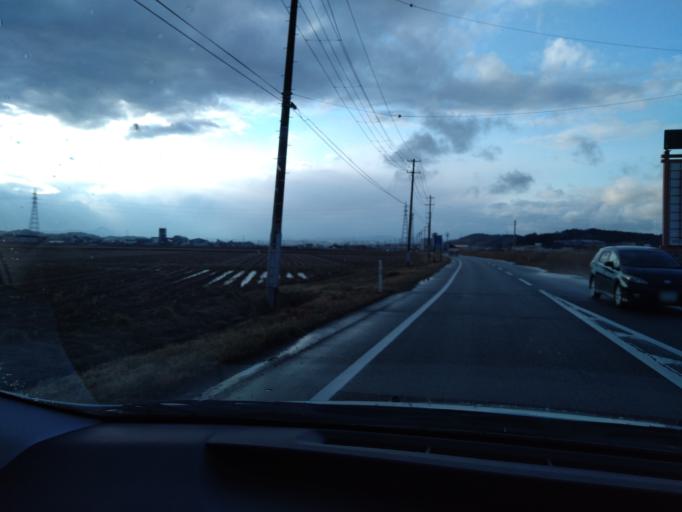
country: JP
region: Iwate
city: Ichinoseki
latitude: 38.7977
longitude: 141.0771
